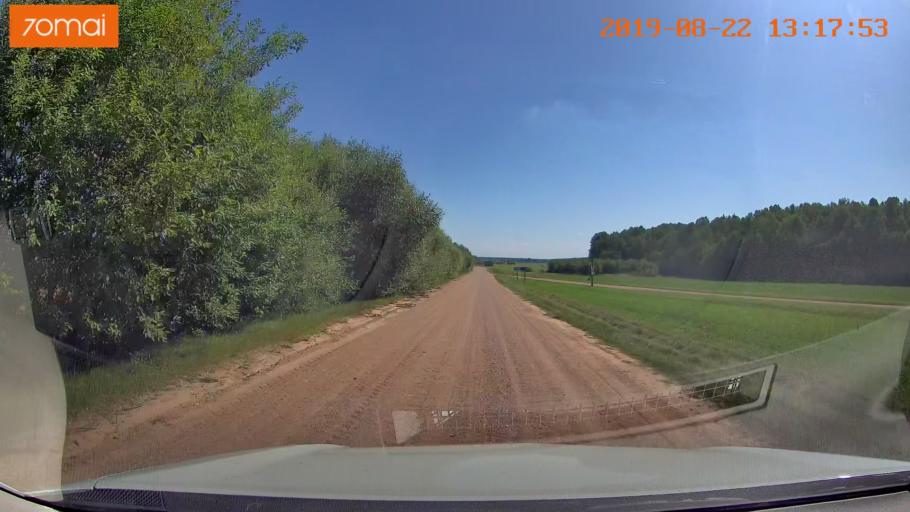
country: BY
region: Minsk
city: Prawdzinski
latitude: 53.2448
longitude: 27.9292
